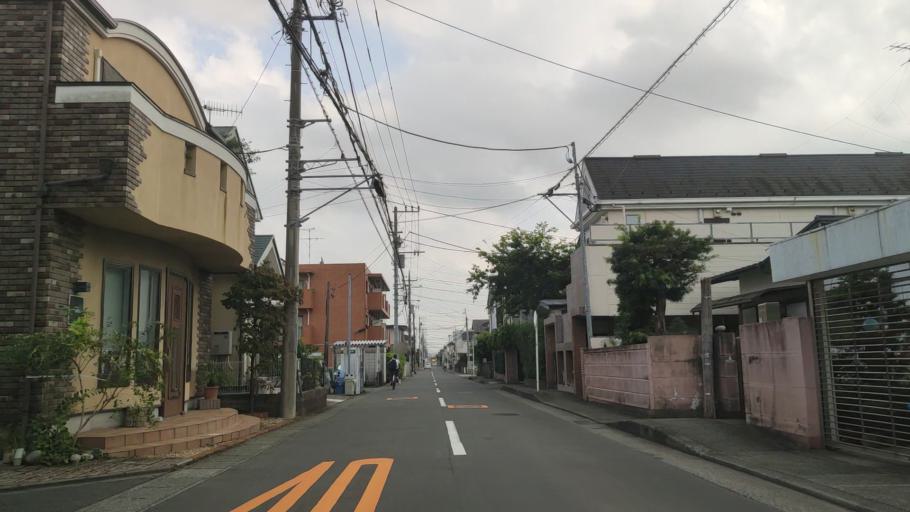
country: JP
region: Kanagawa
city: Minami-rinkan
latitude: 35.4932
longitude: 139.4429
